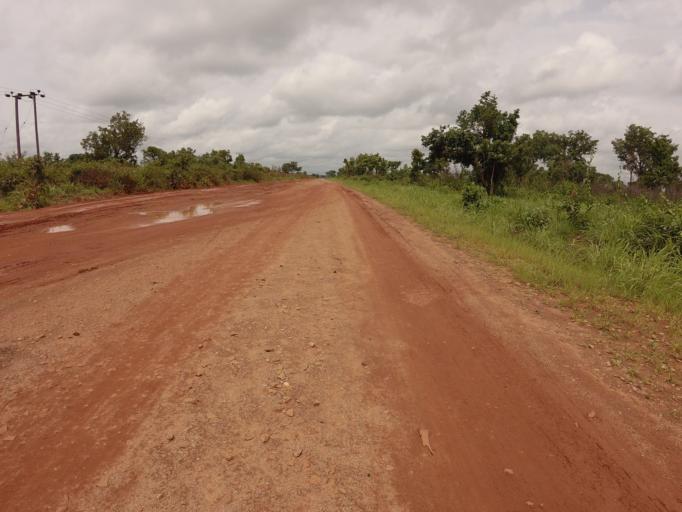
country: GH
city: Kpandae
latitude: 8.4503
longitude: 0.3492
